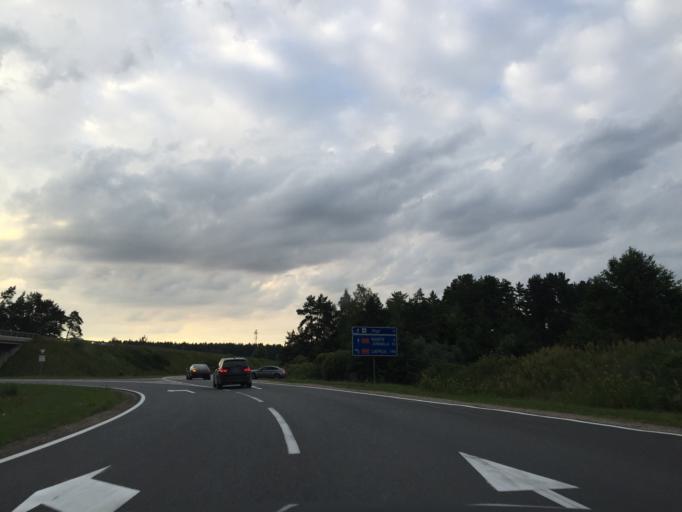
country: LV
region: Babite
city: Pinki
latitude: 56.9225
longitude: 23.9154
